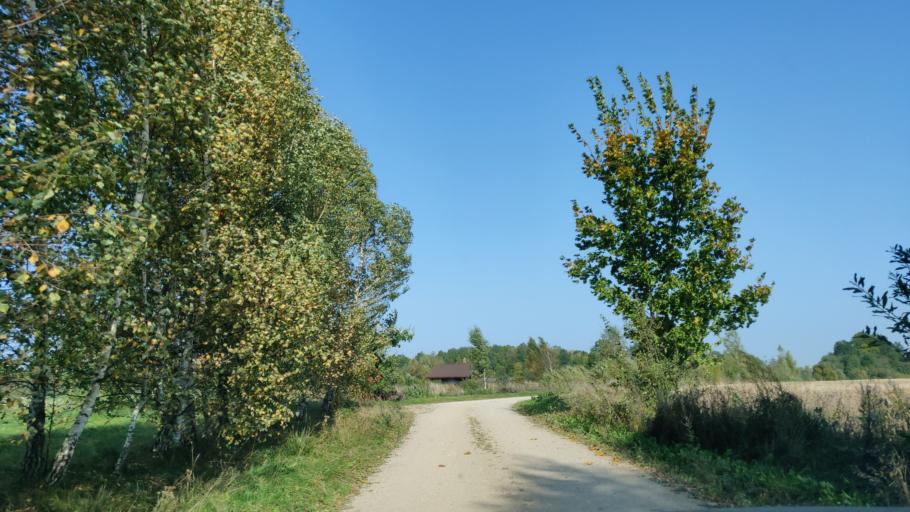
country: LT
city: Sirvintos
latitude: 54.9629
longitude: 24.7853
